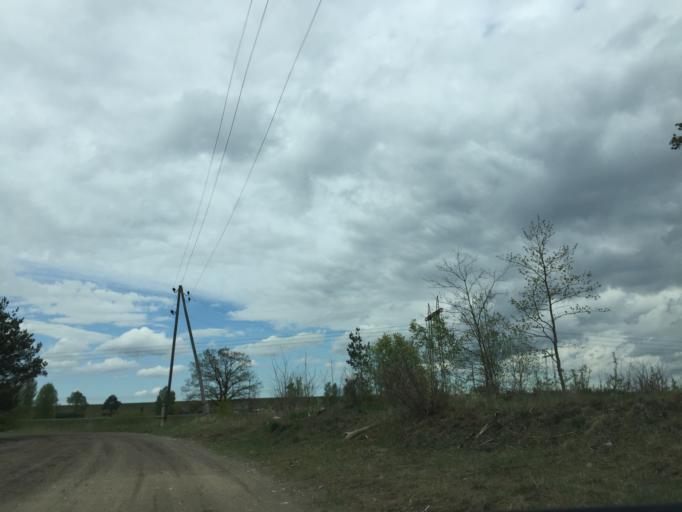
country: LV
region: Kekava
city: Kekava
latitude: 56.8169
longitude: 24.2934
